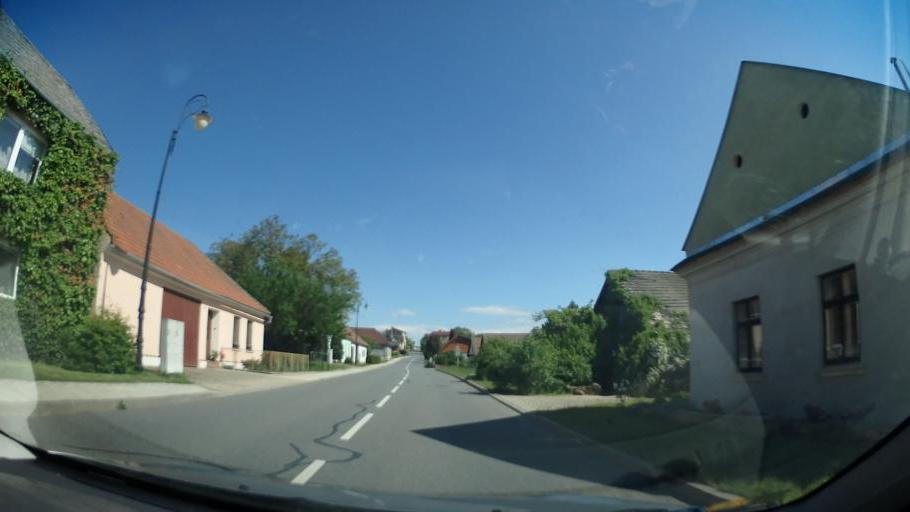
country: CZ
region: South Moravian
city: Velke Opatovice
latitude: 49.6311
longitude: 16.6078
